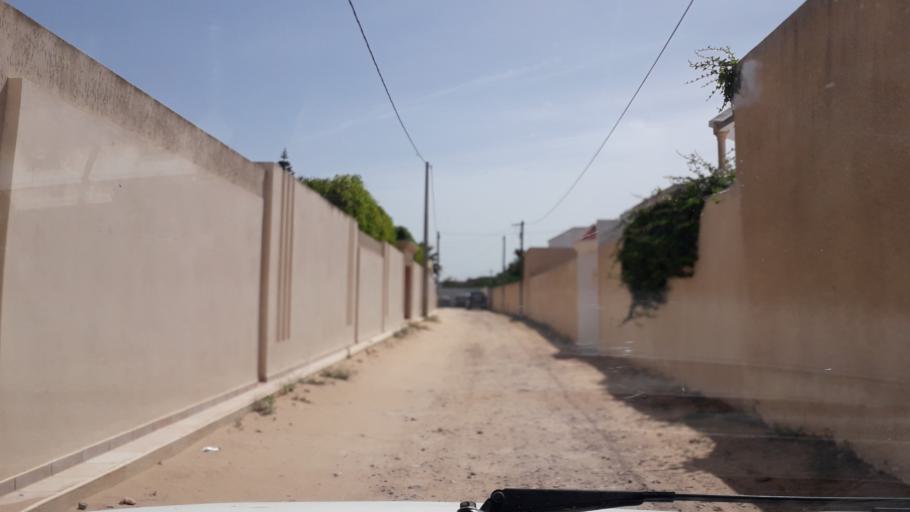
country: TN
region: Safaqis
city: Al Qarmadah
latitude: 34.7979
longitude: 10.7611
